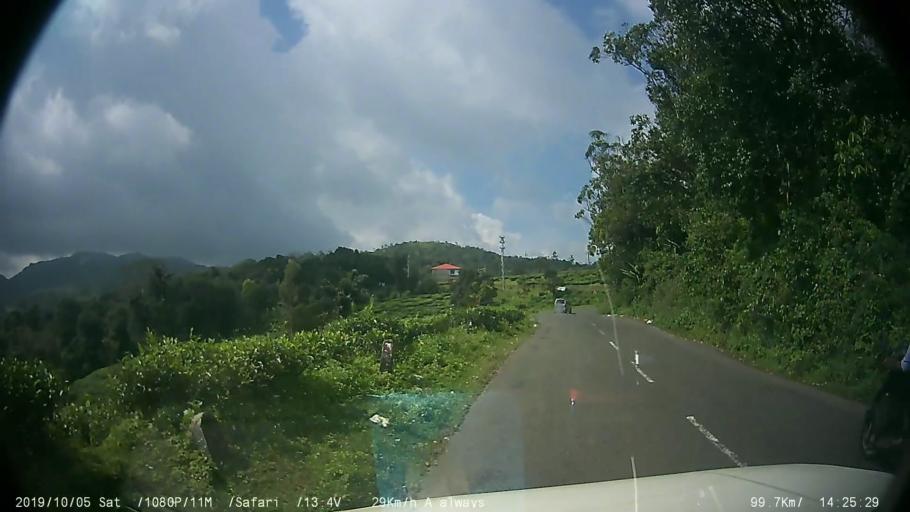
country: IN
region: Kerala
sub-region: Kottayam
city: Erattupetta
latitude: 9.5957
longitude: 76.9695
